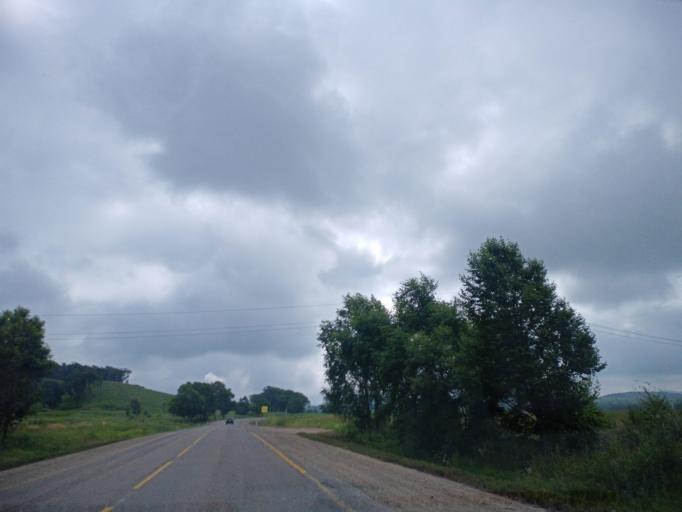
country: RU
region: Primorskiy
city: Dal'nerechensk
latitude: 46.0384
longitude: 133.8804
